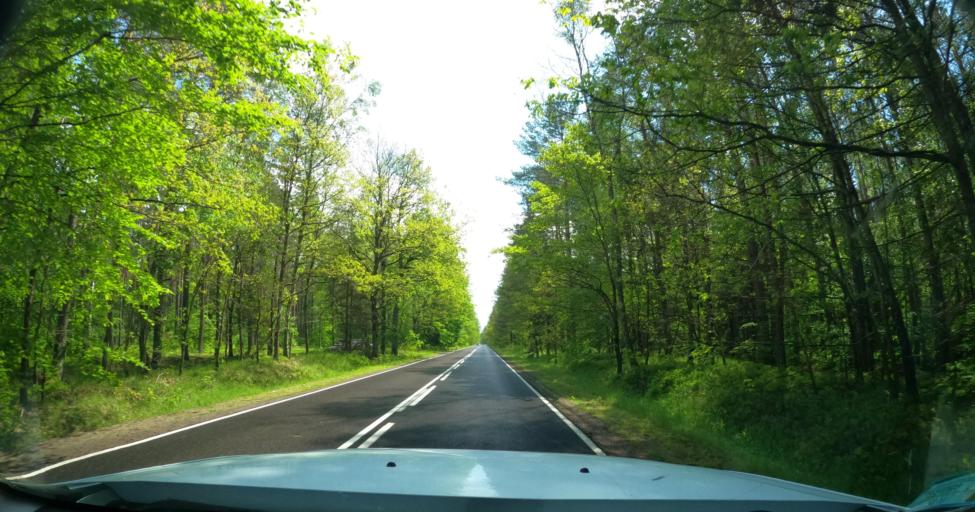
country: PL
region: Pomeranian Voivodeship
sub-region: Powiat slupski
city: Potegowo
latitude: 54.3955
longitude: 17.4695
